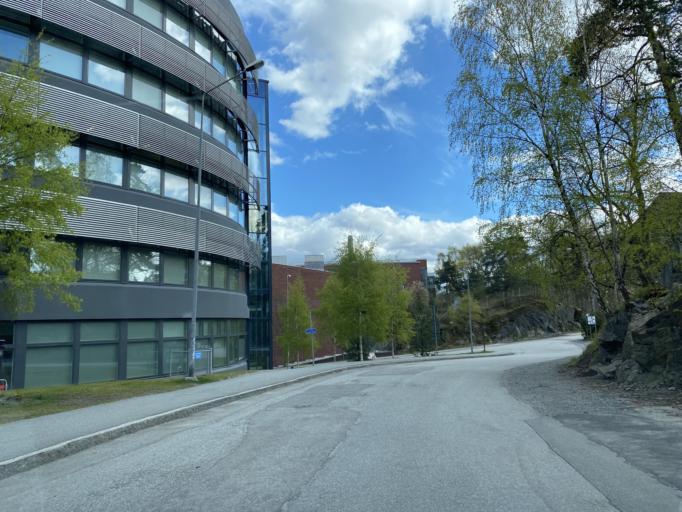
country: SE
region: Stockholm
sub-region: Solna Kommun
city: Solna
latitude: 59.3502
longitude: 18.0215
